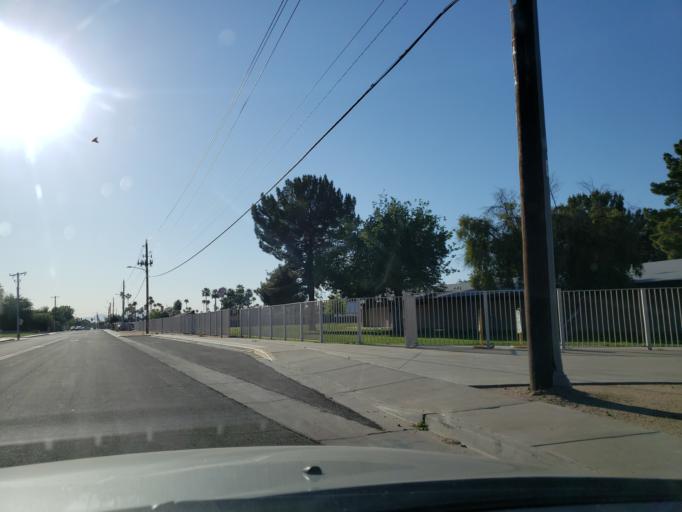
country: US
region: Arizona
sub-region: Maricopa County
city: Glendale
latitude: 33.5422
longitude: -112.1650
